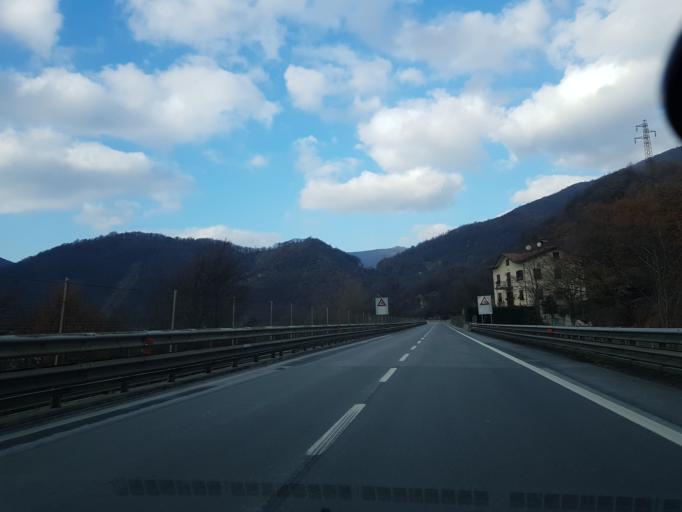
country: IT
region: Liguria
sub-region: Provincia di Genova
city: Isola del Cantone
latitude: 44.6471
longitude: 8.9594
